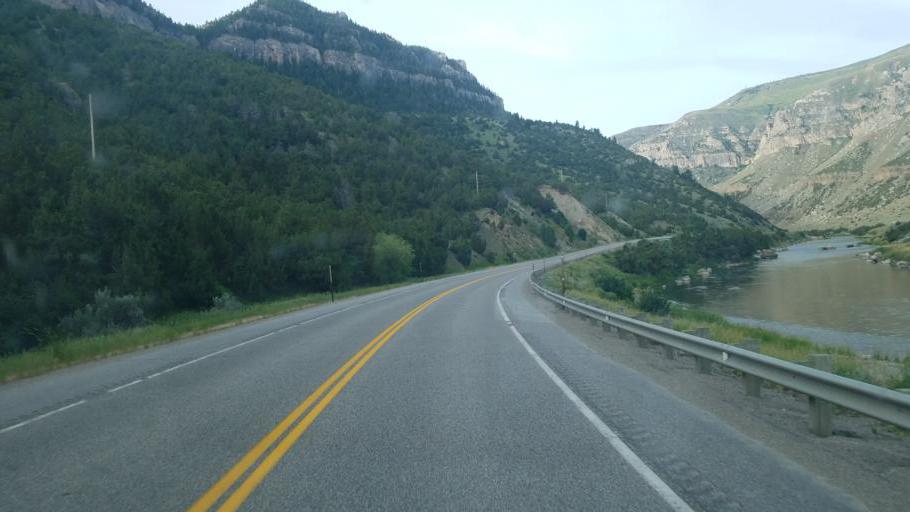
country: US
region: Wyoming
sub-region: Hot Springs County
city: Thermopolis
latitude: 43.4908
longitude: -108.1585
